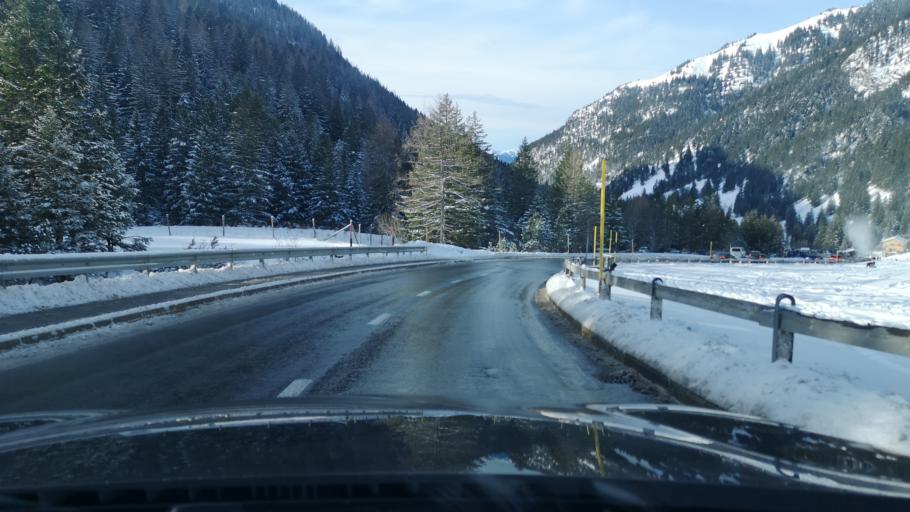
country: LI
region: Triesenberg
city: Triesenberg
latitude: 47.1061
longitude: 9.6034
